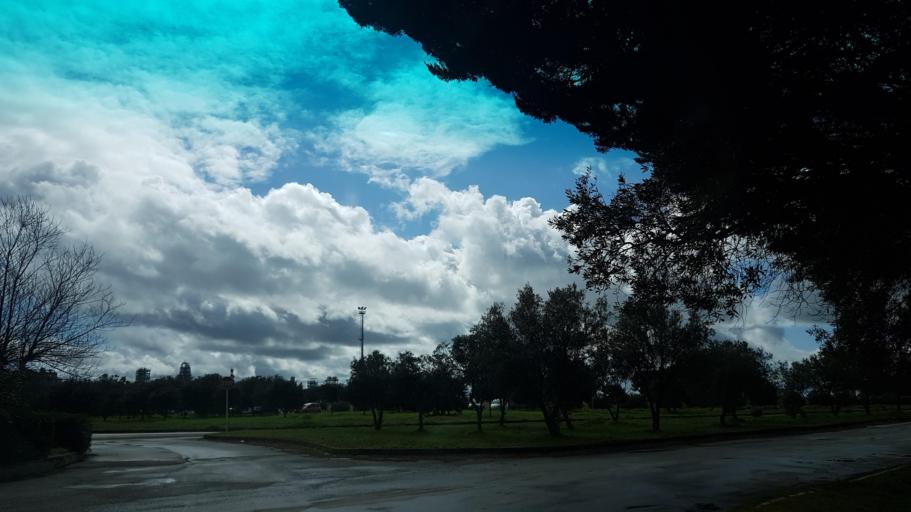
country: IT
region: Apulia
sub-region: Provincia di Brindisi
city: Materdomini
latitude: 40.6450
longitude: 17.9901
